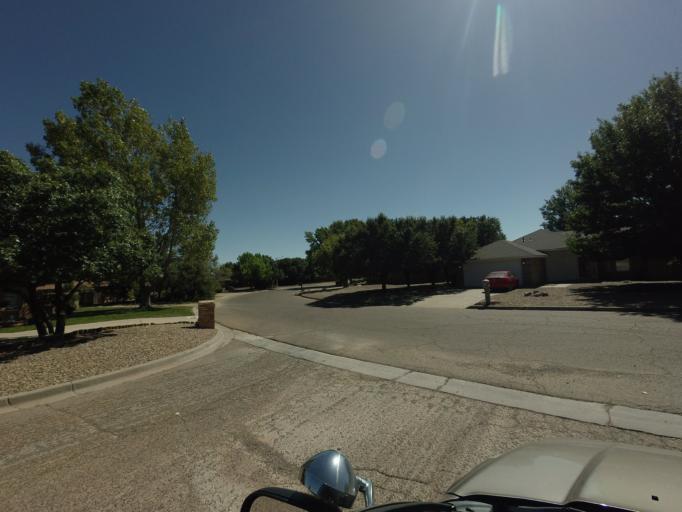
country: US
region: New Mexico
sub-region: Curry County
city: Clovis
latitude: 34.4437
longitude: -103.1810
